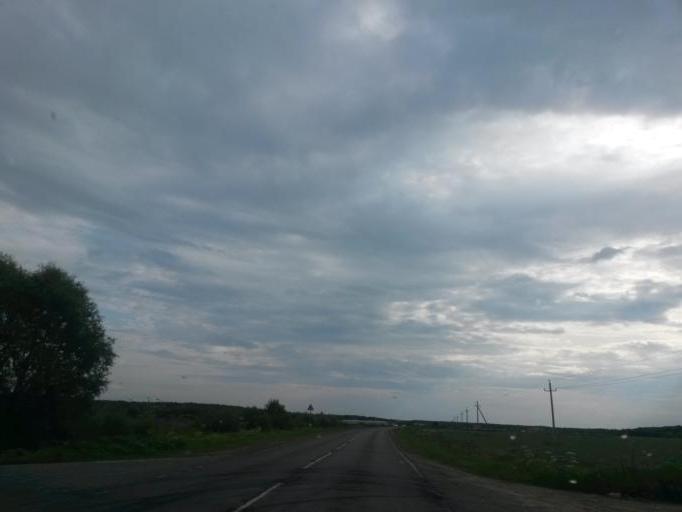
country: RU
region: Moskovskaya
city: Belyye Stolby
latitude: 55.2999
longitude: 37.8014
